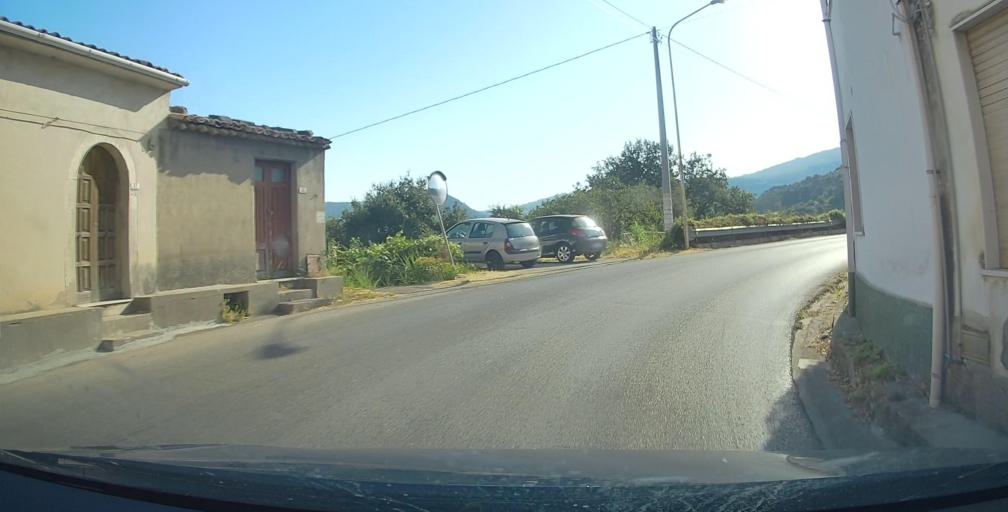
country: IT
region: Sicily
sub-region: Messina
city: Librizzi
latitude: 38.0778
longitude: 14.9745
